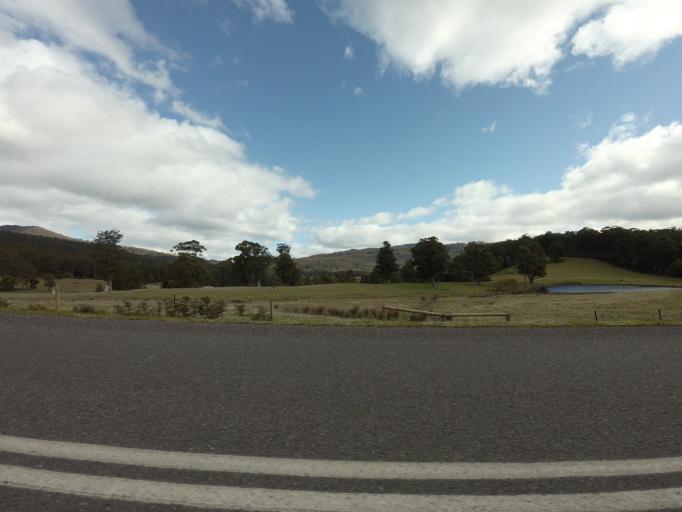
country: AU
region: Tasmania
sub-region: Huon Valley
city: Geeveston
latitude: -43.1963
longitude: 146.9436
